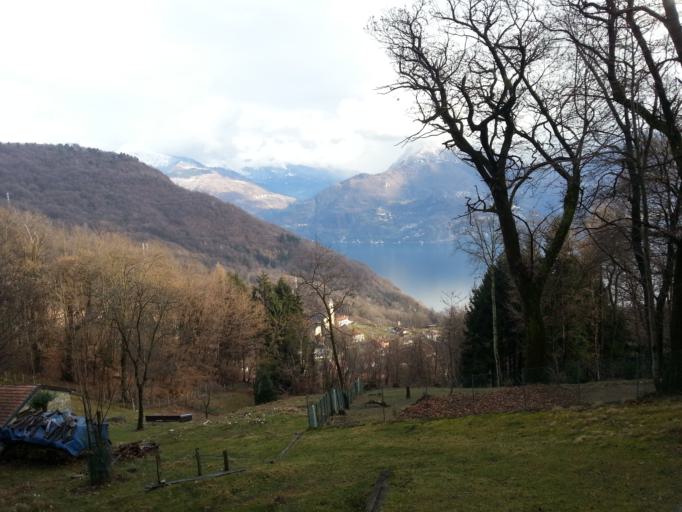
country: IT
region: Lombardy
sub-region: Provincia di Como
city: Plesio
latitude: 46.0454
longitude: 9.2238
